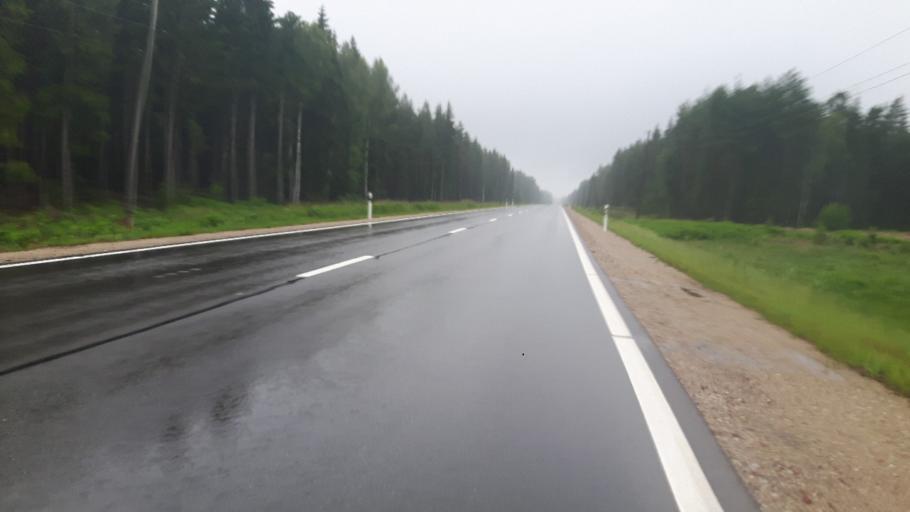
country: LV
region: Rucavas
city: Rucava
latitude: 56.1666
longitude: 21.1449
